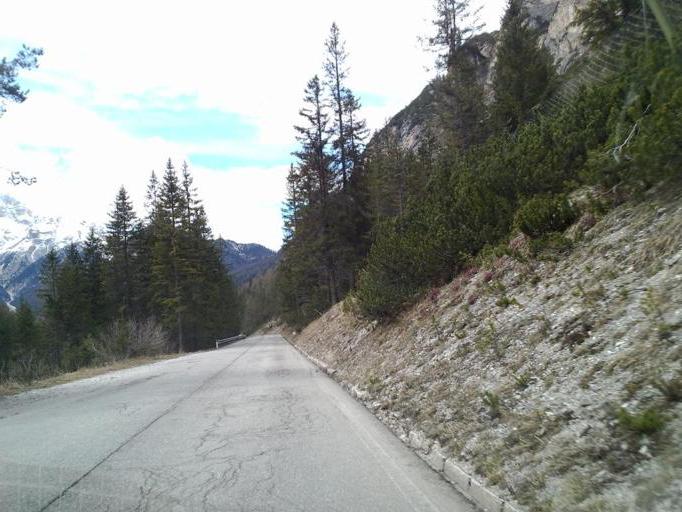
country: IT
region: Veneto
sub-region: Provincia di Belluno
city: Cortina d'Ampezzo
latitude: 46.6072
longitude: 12.2370
